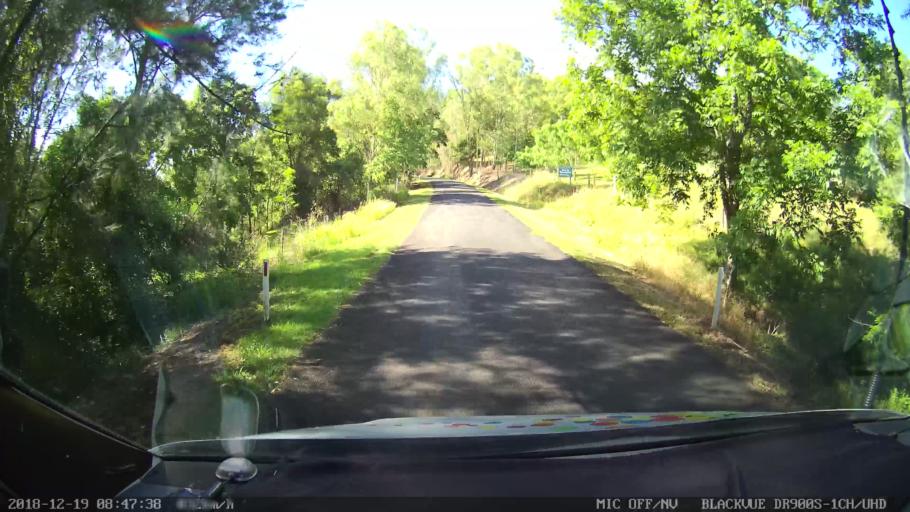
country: AU
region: New South Wales
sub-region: Kyogle
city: Kyogle
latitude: -28.3681
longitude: 152.9713
